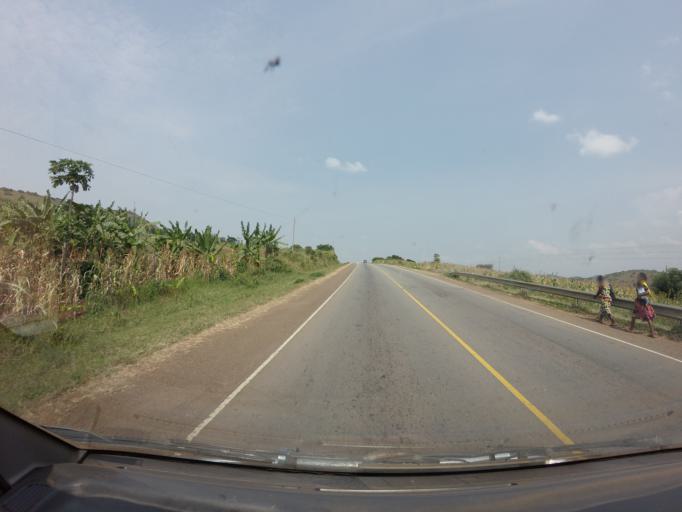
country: UG
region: Central Region
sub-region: Lwengo District
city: Lwengo
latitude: -0.4024
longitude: 31.3598
